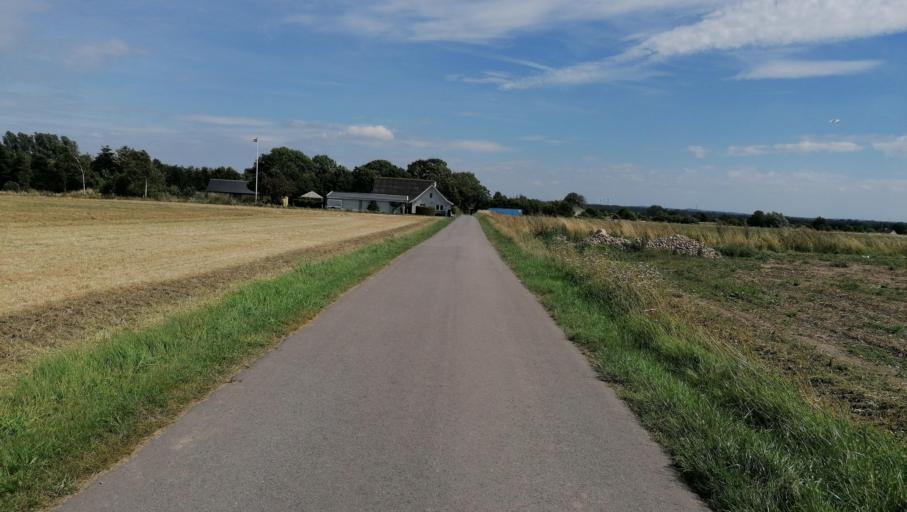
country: DK
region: Zealand
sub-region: Odsherred Kommune
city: Horve
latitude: 55.7644
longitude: 11.4587
